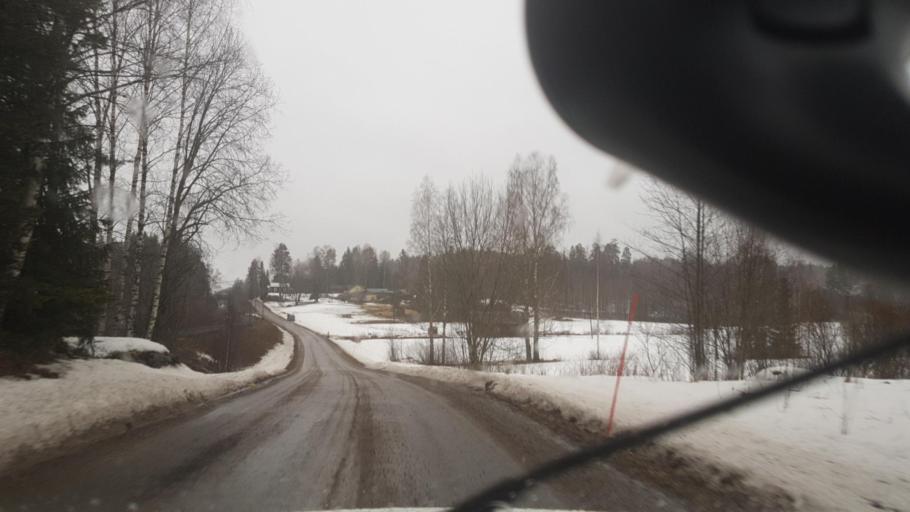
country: SE
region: Vaermland
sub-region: Eda Kommun
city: Amotfors
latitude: 59.8207
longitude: 12.3643
